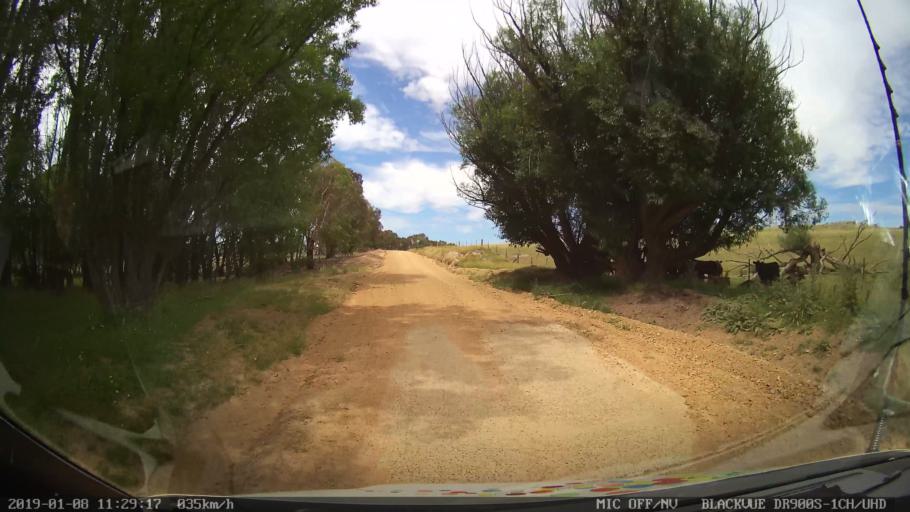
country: AU
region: New South Wales
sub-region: Guyra
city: Guyra
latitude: -30.2995
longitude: 151.5486
